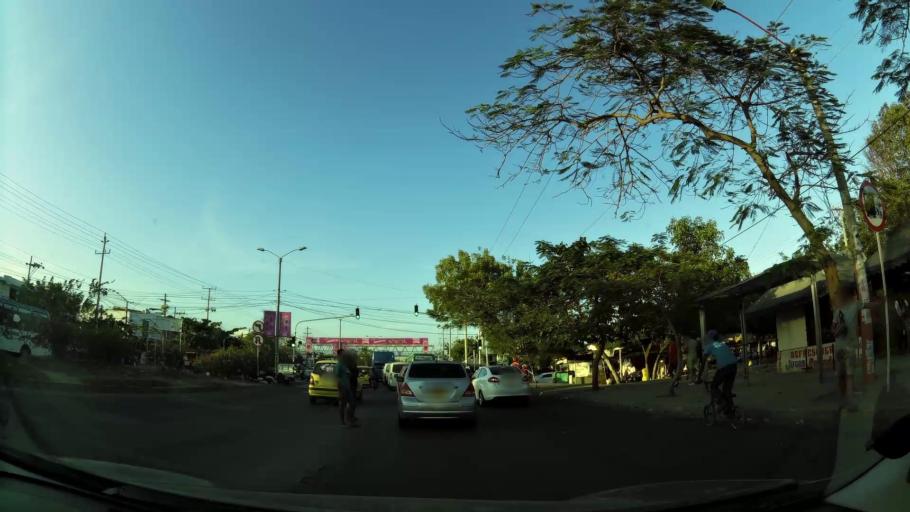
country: CO
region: Atlantico
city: Soledad
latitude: 10.9168
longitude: -74.7990
